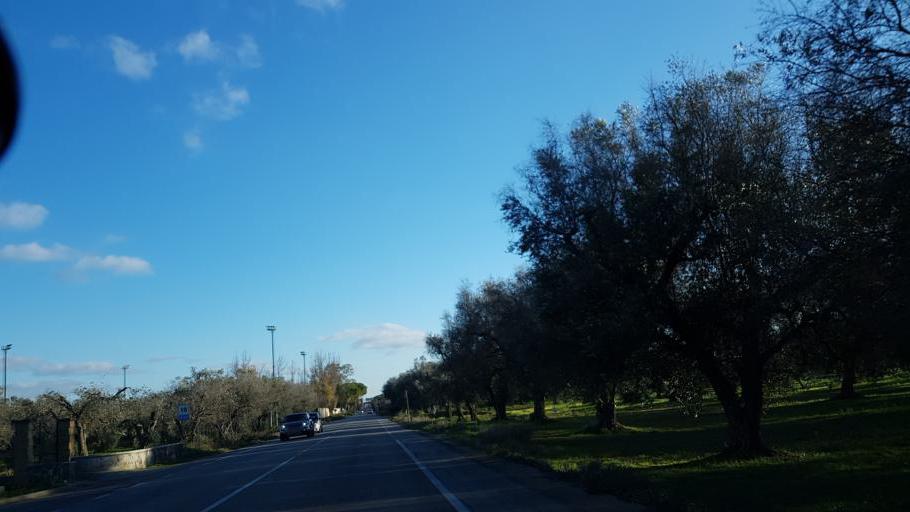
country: IT
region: Apulia
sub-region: Provincia di Lecce
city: Squinzano
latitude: 40.4463
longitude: 18.0318
